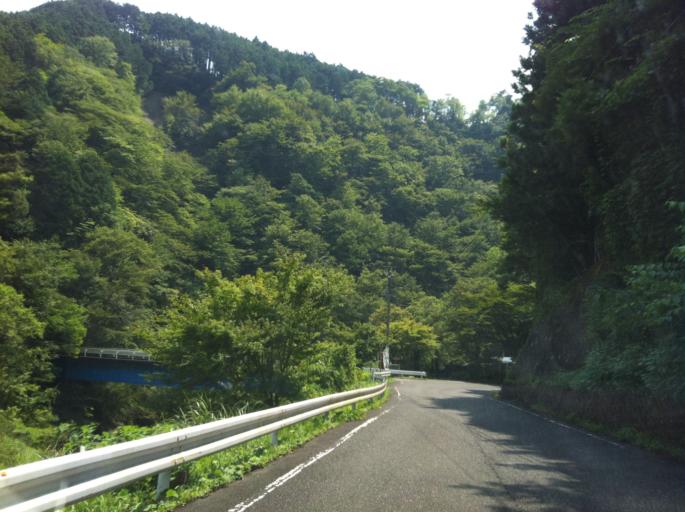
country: JP
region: Shizuoka
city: Fujinomiya
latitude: 35.2782
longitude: 138.3326
